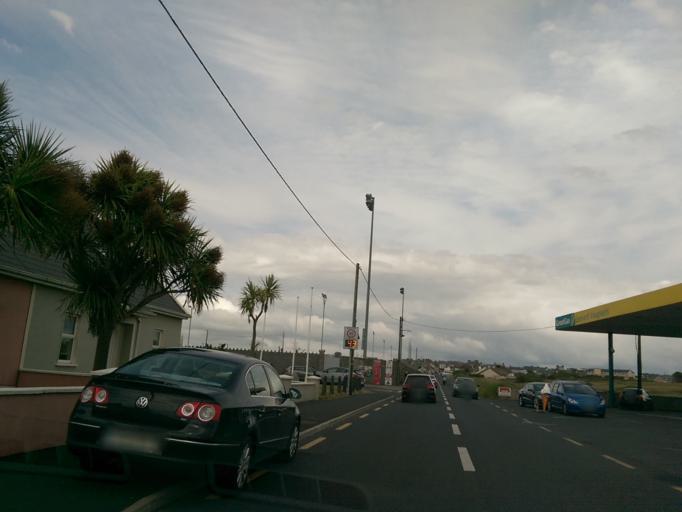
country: IE
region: Munster
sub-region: An Clar
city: Kilrush
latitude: 52.8512
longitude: -9.4094
